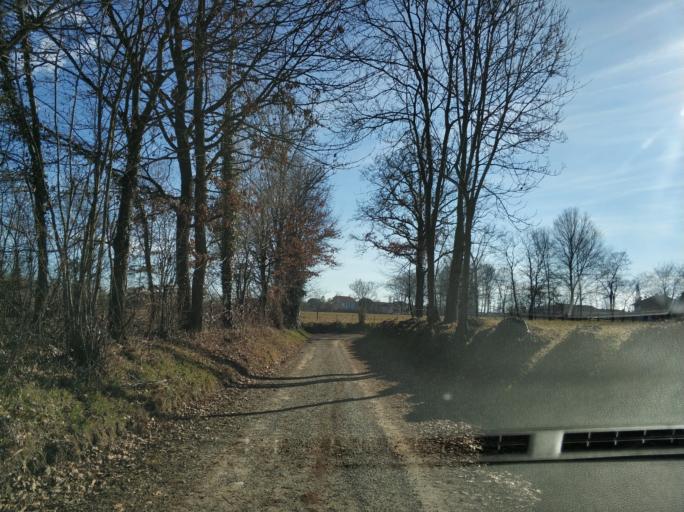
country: IT
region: Piedmont
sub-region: Provincia di Torino
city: San Carlo Canavese
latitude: 45.2538
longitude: 7.6070
